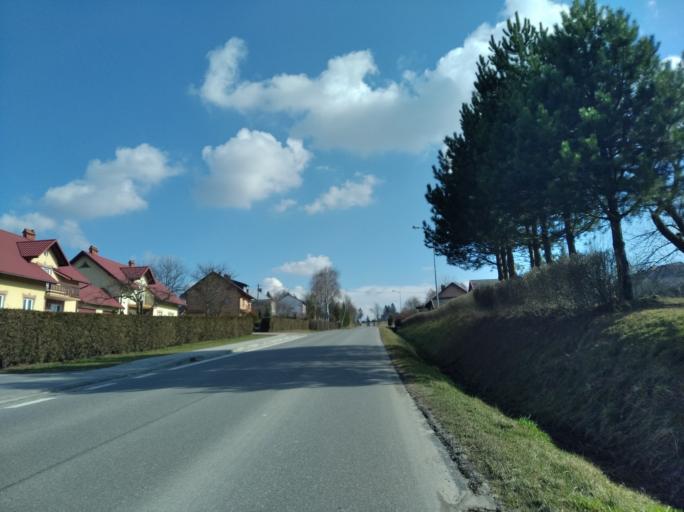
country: PL
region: Subcarpathian Voivodeship
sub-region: Powiat strzyzowski
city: Frysztak
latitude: 49.8502
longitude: 21.5189
